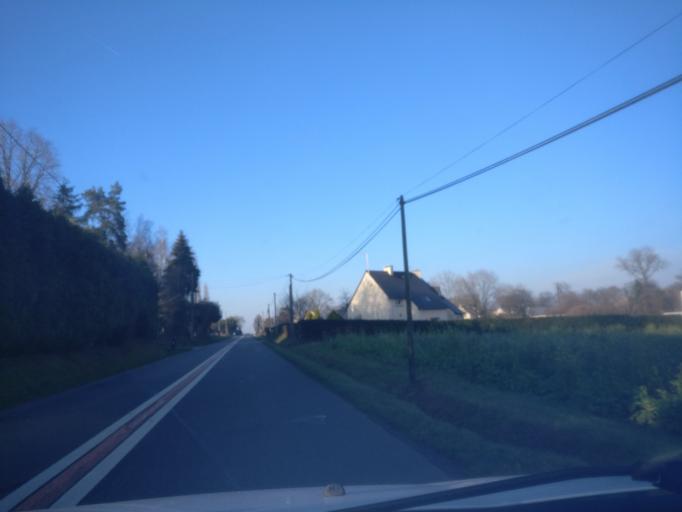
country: FR
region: Brittany
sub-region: Departement d'Ille-et-Vilaine
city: Livre-sur-Changeon
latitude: 48.1990
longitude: -1.3306
